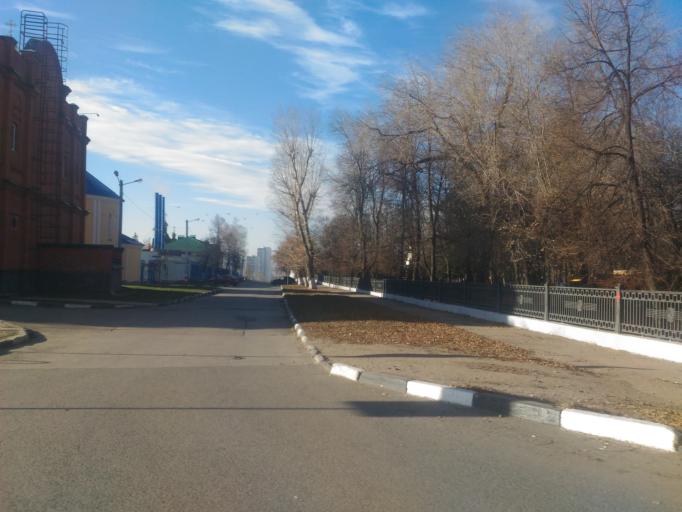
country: RU
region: Ulyanovsk
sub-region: Ulyanovskiy Rayon
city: Ulyanovsk
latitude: 54.3078
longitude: 48.3785
